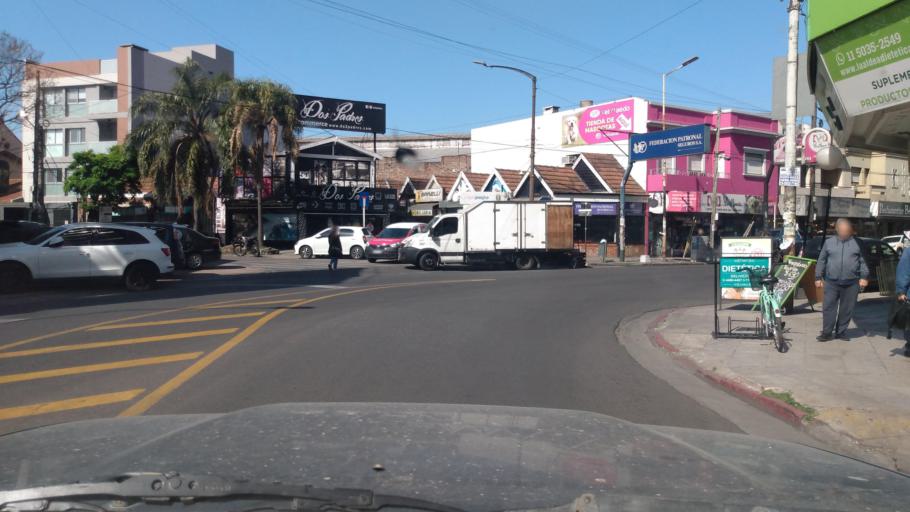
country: AR
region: Buenos Aires
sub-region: Partido de Moron
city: Moron
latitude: -34.6456
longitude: -58.5907
